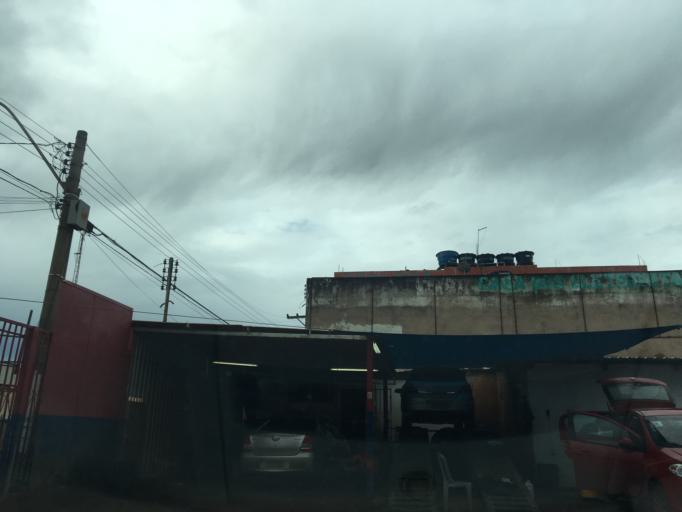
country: BR
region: Goias
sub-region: Luziania
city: Luziania
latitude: -16.0261
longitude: -48.0609
